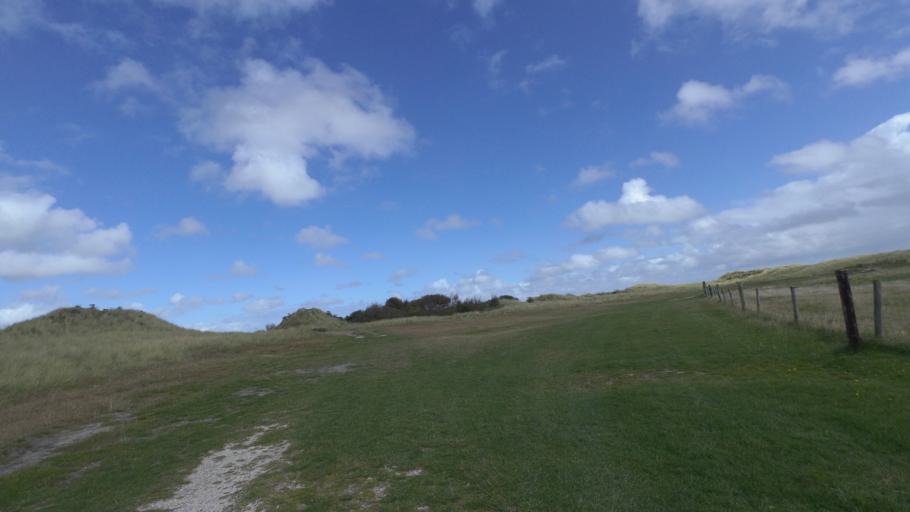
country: NL
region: Friesland
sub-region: Gemeente Ameland
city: Nes
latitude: 53.4476
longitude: 5.8580
